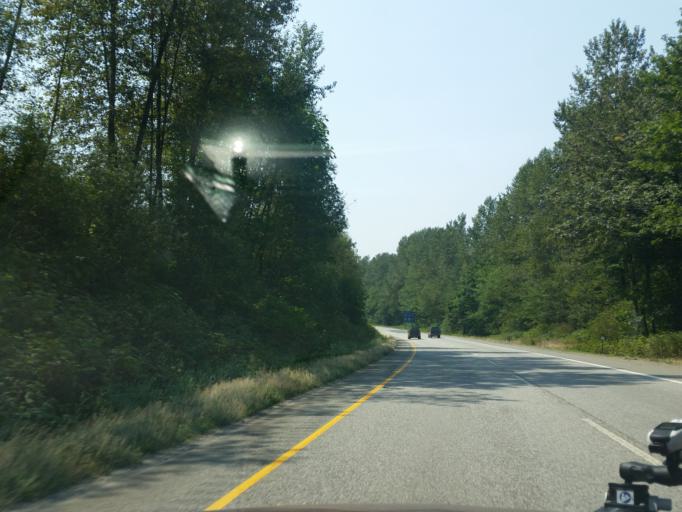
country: CA
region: British Columbia
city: Agassiz
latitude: 49.2148
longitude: -121.7003
